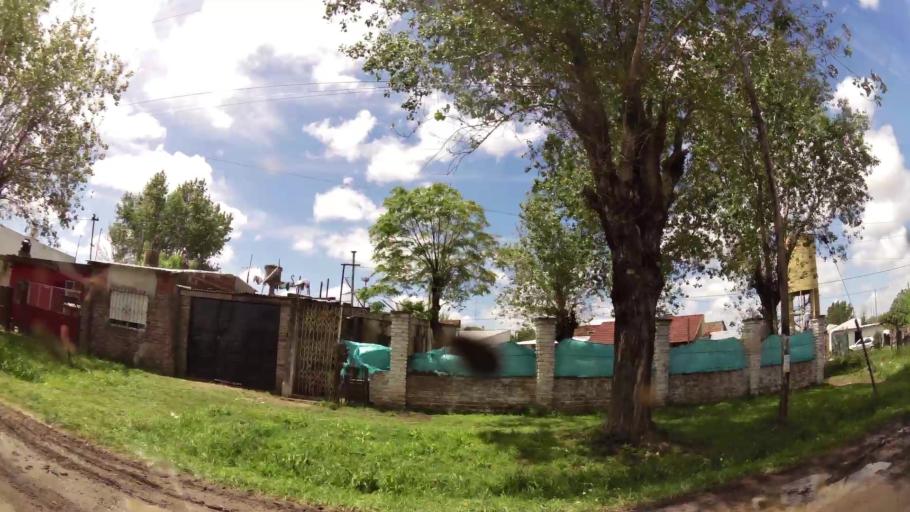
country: AR
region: Buenos Aires
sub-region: Partido de Quilmes
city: Quilmes
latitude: -34.8269
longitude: -58.2321
